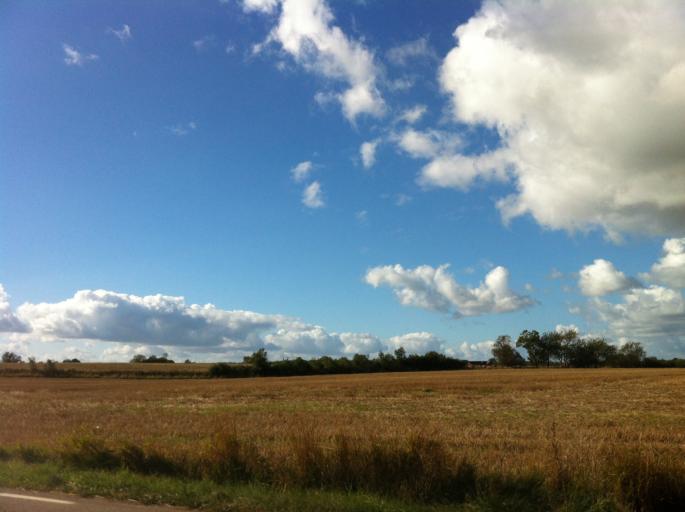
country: SE
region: Skane
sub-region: Sjobo Kommun
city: Sjoebo
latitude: 55.6524
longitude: 13.8125
